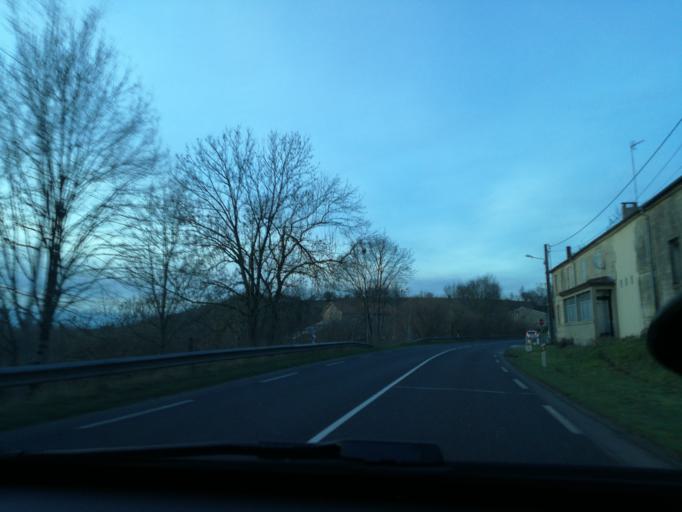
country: FR
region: Lorraine
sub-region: Departement de la Meuse
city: Fains-Veel
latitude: 48.8092
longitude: 5.1105
